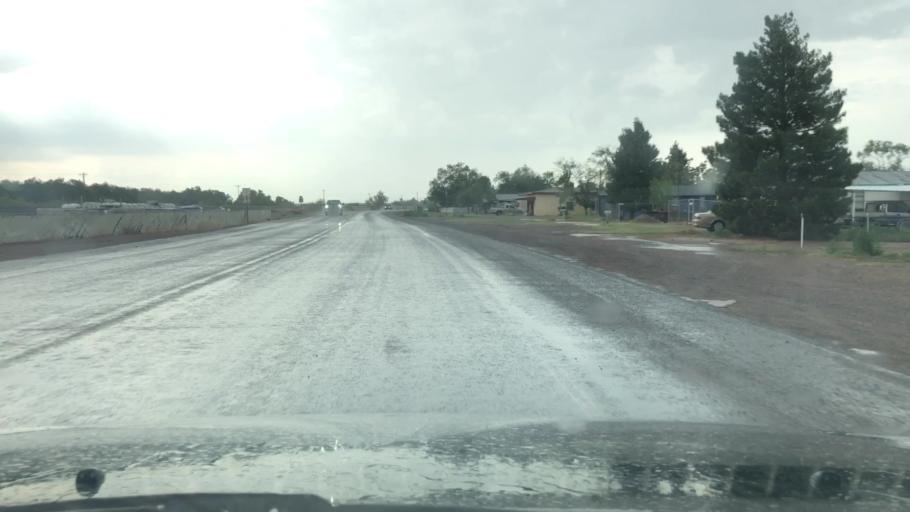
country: US
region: New Mexico
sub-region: Dona Ana County
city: Vado
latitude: 32.1160
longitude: -106.6653
